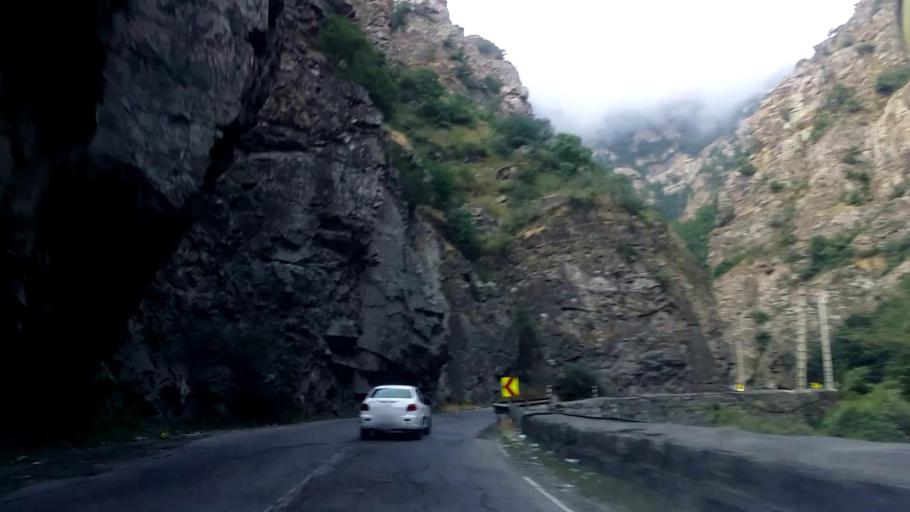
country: IR
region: Mazandaran
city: Chalus
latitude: 36.2968
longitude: 51.2461
